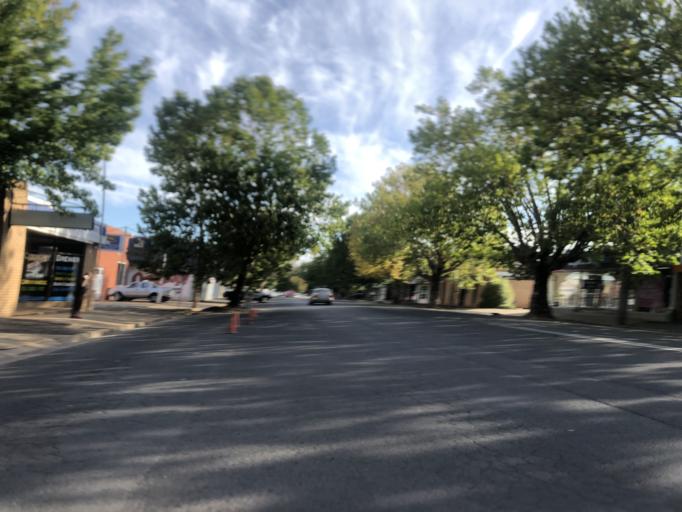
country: AU
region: New South Wales
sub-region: Orange Municipality
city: Orange
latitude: -33.2876
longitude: 149.1003
